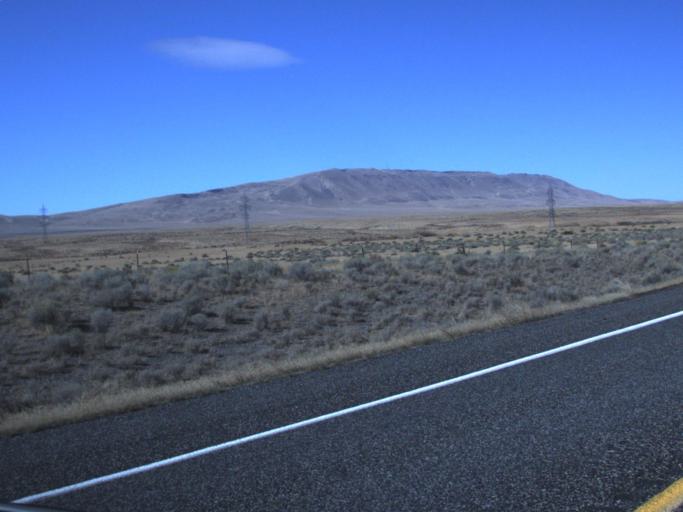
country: US
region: Washington
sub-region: Benton County
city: West Richland
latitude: 46.3887
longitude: -119.4327
